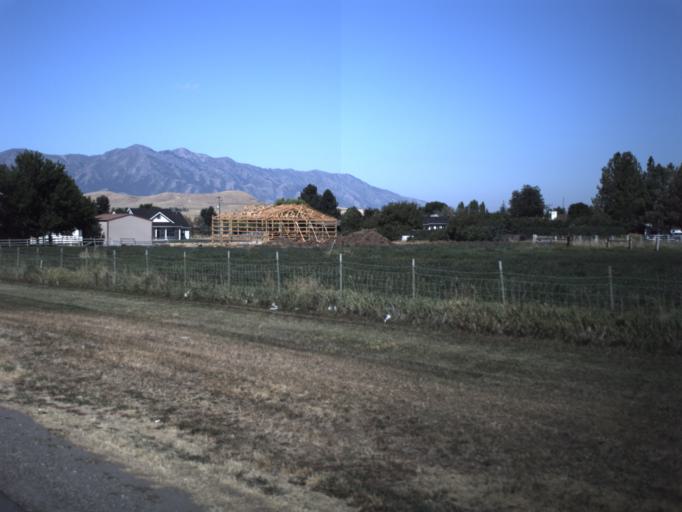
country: US
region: Utah
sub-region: Cache County
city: Hyrum
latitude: 41.5665
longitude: -111.8308
